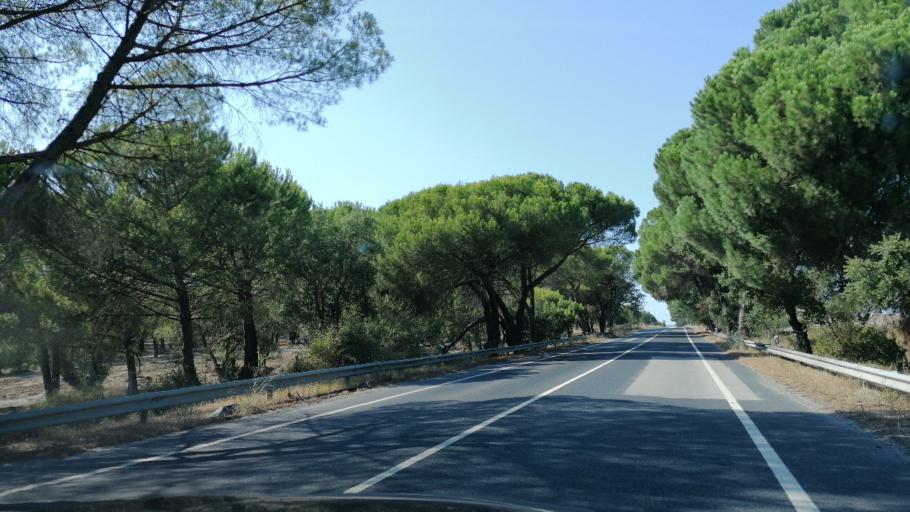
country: PT
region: Evora
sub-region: Vendas Novas
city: Vendas Novas
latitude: 38.7063
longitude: -8.6136
